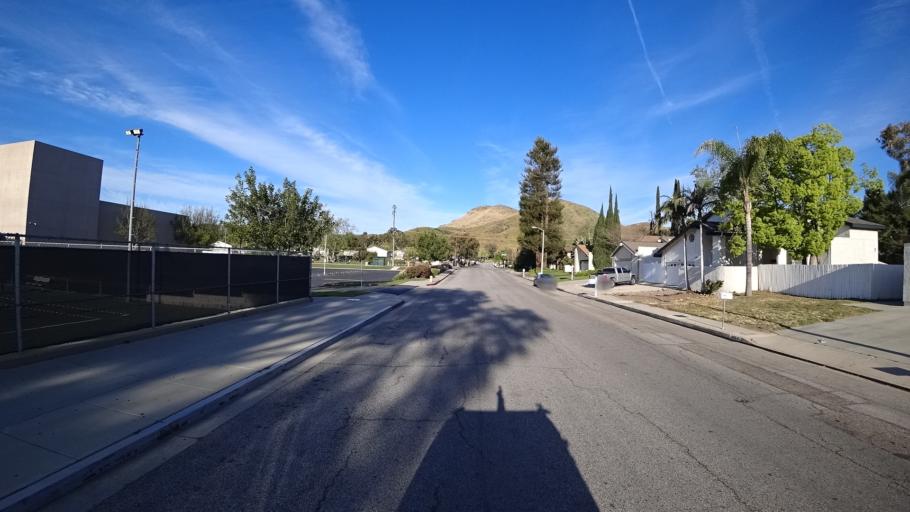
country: US
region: California
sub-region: Ventura County
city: Casa Conejo
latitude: 34.1863
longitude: -118.9528
